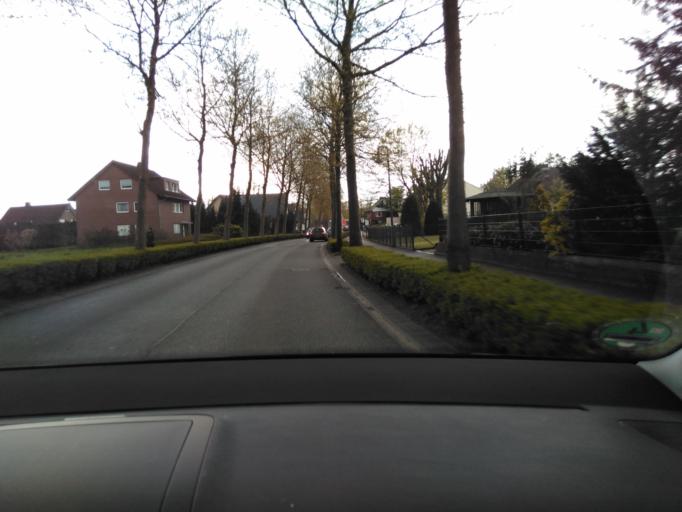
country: DE
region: North Rhine-Westphalia
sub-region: Regierungsbezirk Detmold
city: Guetersloh
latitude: 51.9322
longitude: 8.4433
